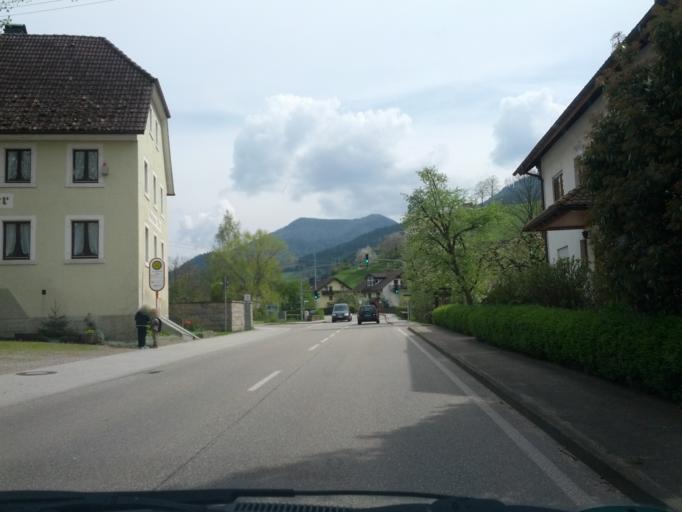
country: DE
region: Baden-Wuerttemberg
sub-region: Freiburg Region
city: Gutach im Breisgau
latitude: 48.1132
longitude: 8.0302
